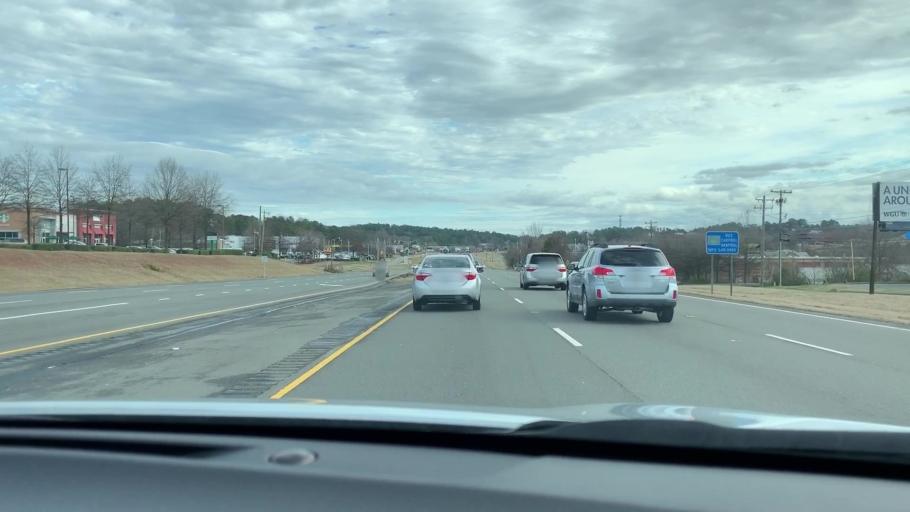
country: US
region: North Carolina
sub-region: Durham County
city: Durham
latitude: 35.9688
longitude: -78.9606
